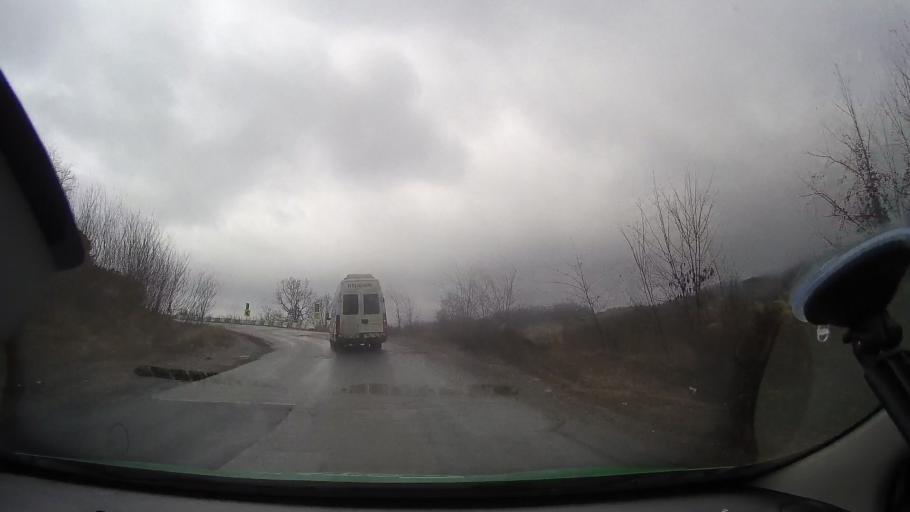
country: RO
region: Arad
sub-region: Comuna Halmagiu
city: Halmagiu
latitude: 46.2859
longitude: 22.5472
